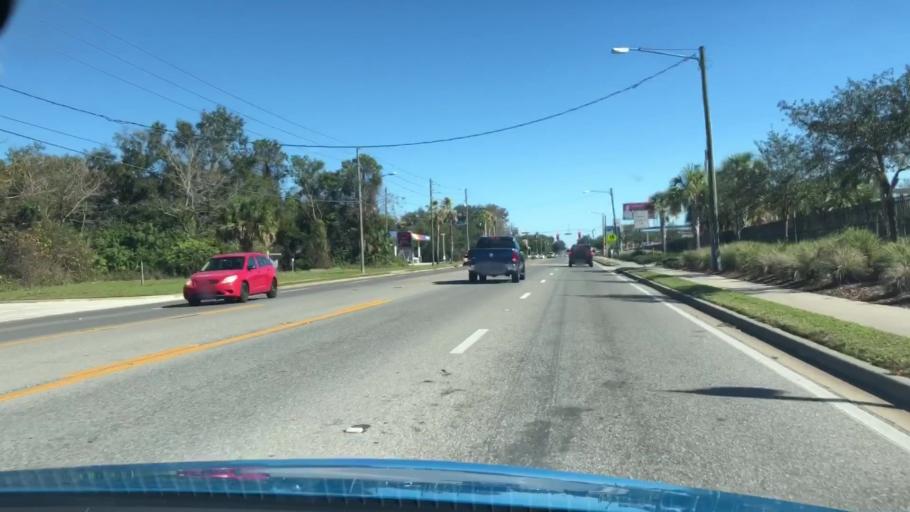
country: US
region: Florida
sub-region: Orange County
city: Sky Lake
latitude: 28.4726
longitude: -81.3863
